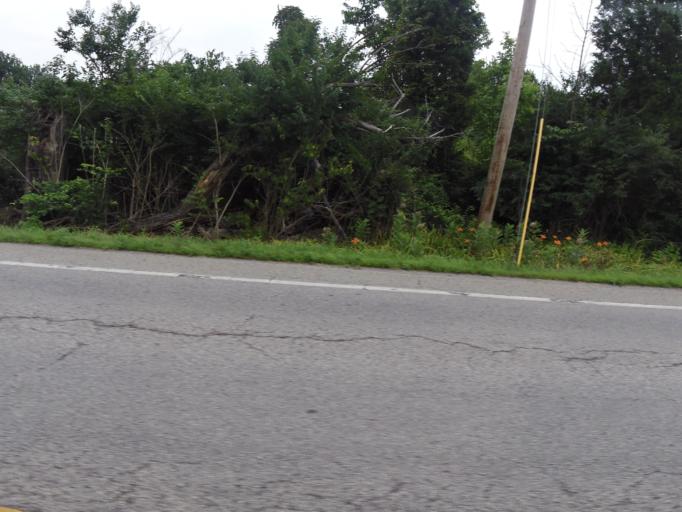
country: US
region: Ohio
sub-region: Brown County
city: Mount Orab
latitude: 39.0677
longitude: -83.9255
